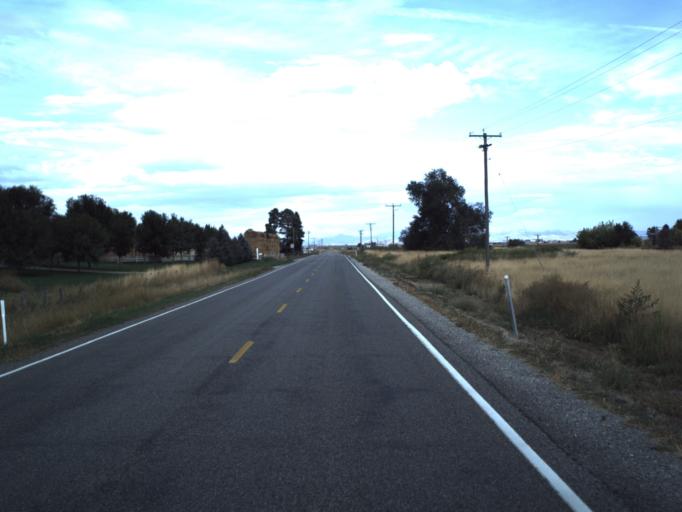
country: US
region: Utah
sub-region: Cache County
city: Lewiston
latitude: 41.9947
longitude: -111.9548
